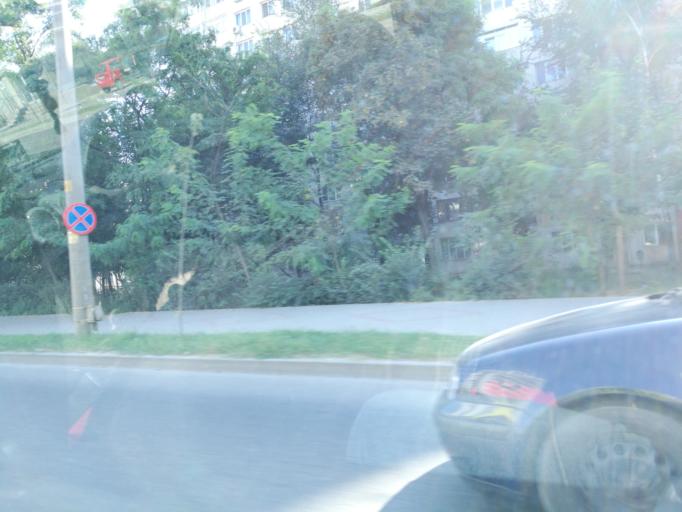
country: RO
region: Iasi
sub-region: Municipiul Iasi
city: Iasi
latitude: 47.1687
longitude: 27.5659
